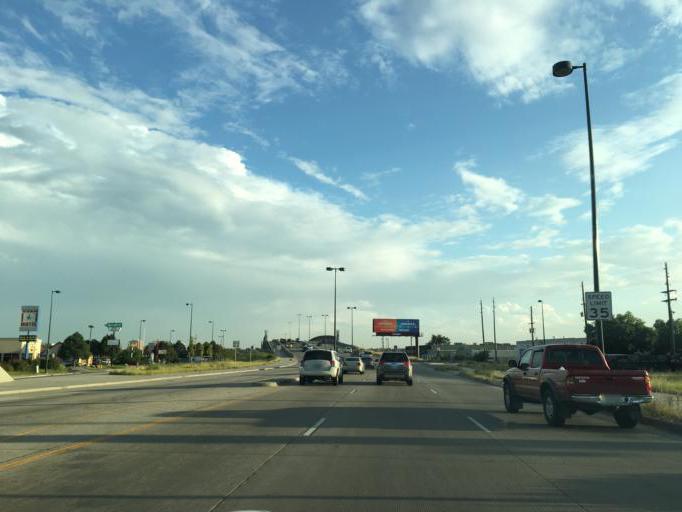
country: US
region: Colorado
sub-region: Adams County
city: Aurora
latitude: 39.7705
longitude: -104.8472
